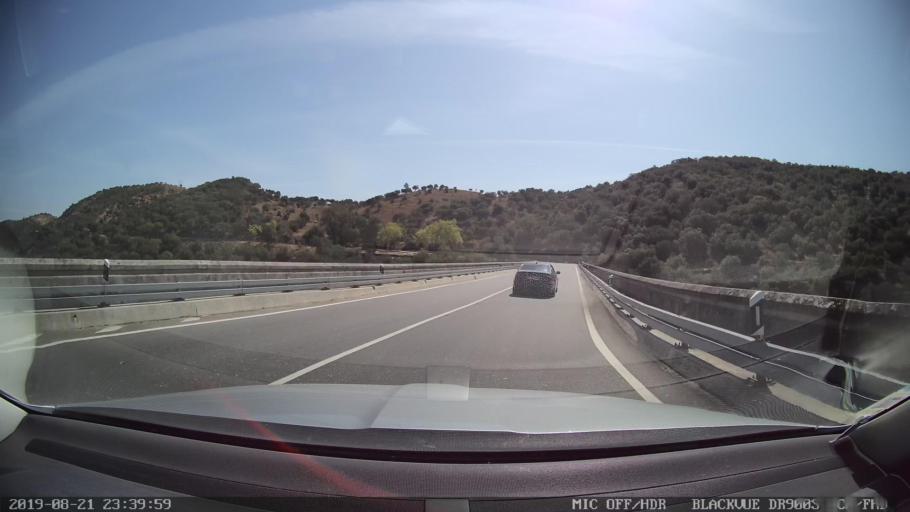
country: PT
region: Castelo Branco
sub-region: Idanha-A-Nova
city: Idanha-a-Nova
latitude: 39.8586
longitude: -7.3343
